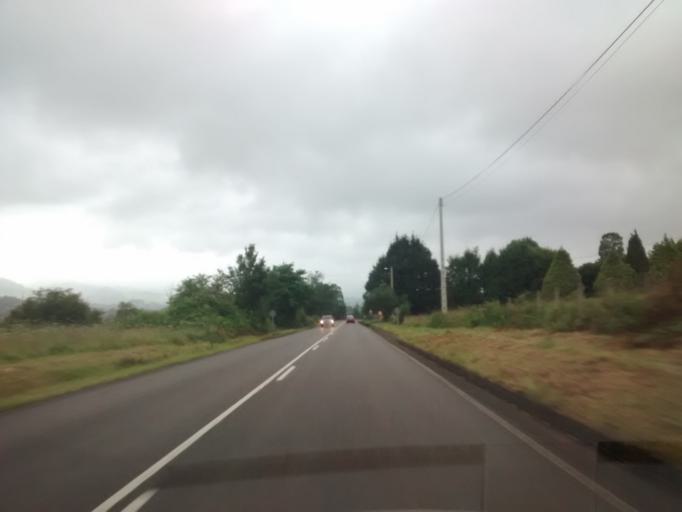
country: ES
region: Asturias
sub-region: Province of Asturias
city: Villaviciosa
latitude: 43.4966
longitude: -5.4277
